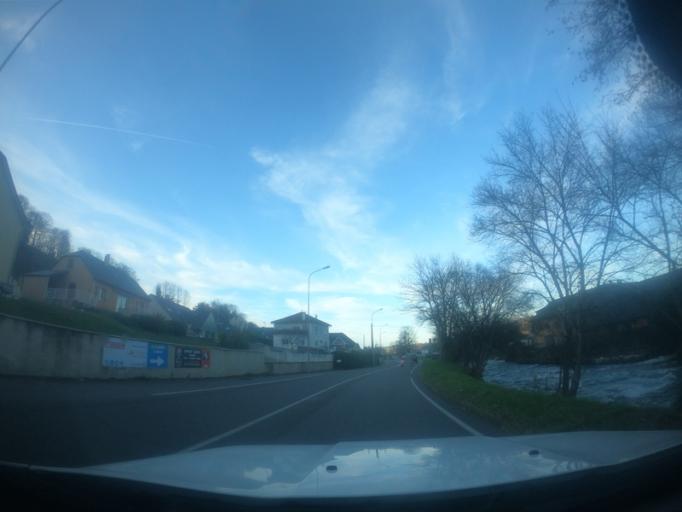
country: FR
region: Midi-Pyrenees
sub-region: Departement des Hautes-Pyrenees
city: Gerde
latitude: 43.0531
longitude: 0.1572
